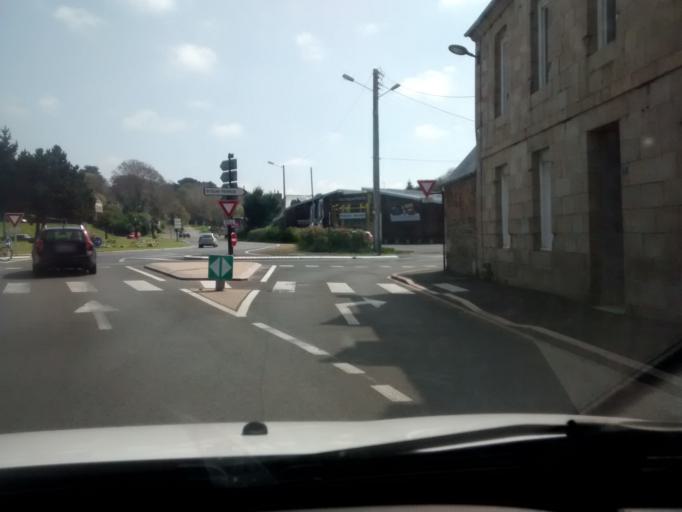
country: FR
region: Brittany
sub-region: Departement des Cotes-d'Armor
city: Perros-Guirec
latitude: 48.7983
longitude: -3.4420
